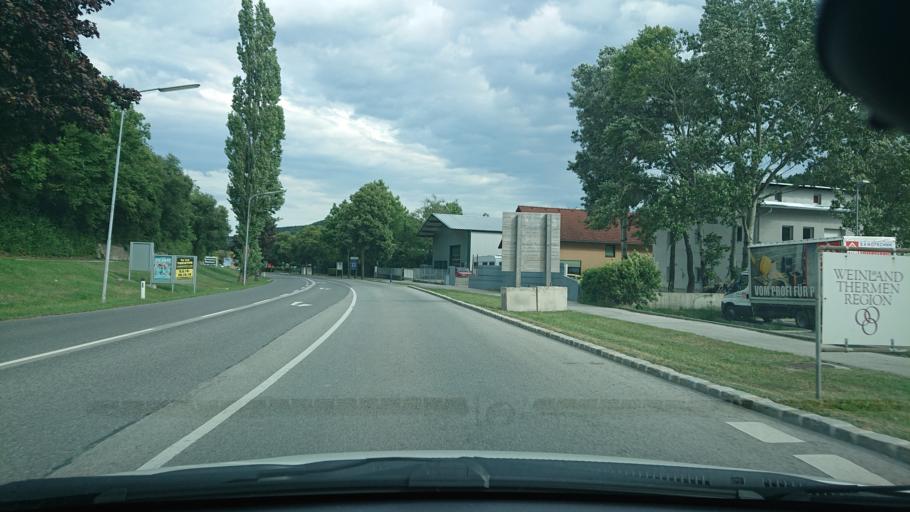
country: AT
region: Lower Austria
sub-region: Politischer Bezirk Baden
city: Berndorf
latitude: 47.9406
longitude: 16.1378
